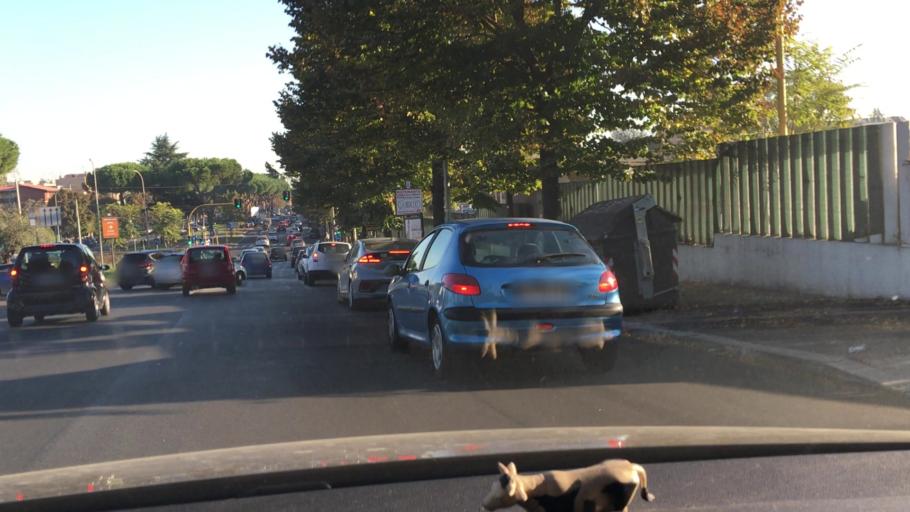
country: IT
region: Latium
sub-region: Citta metropolitana di Roma Capitale
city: Rome
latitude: 41.8731
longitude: 12.5694
